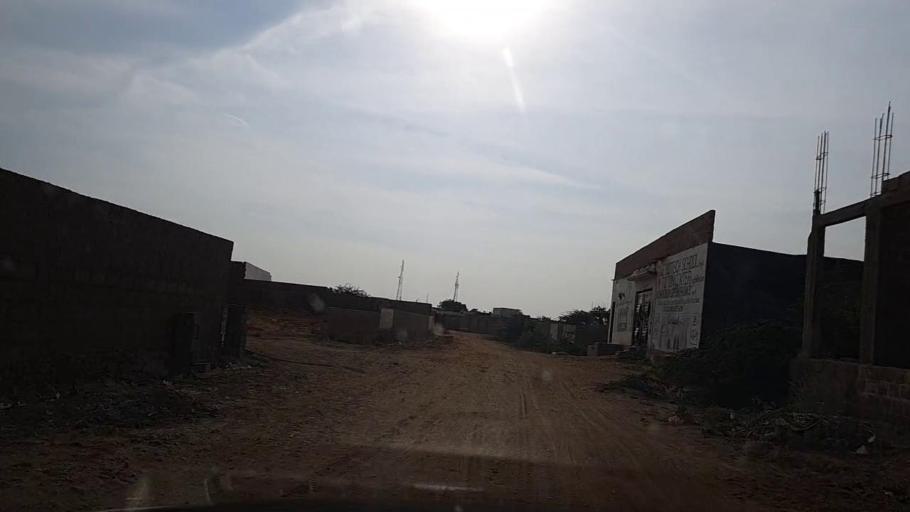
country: PK
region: Sindh
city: Gharo
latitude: 24.7942
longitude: 67.5327
